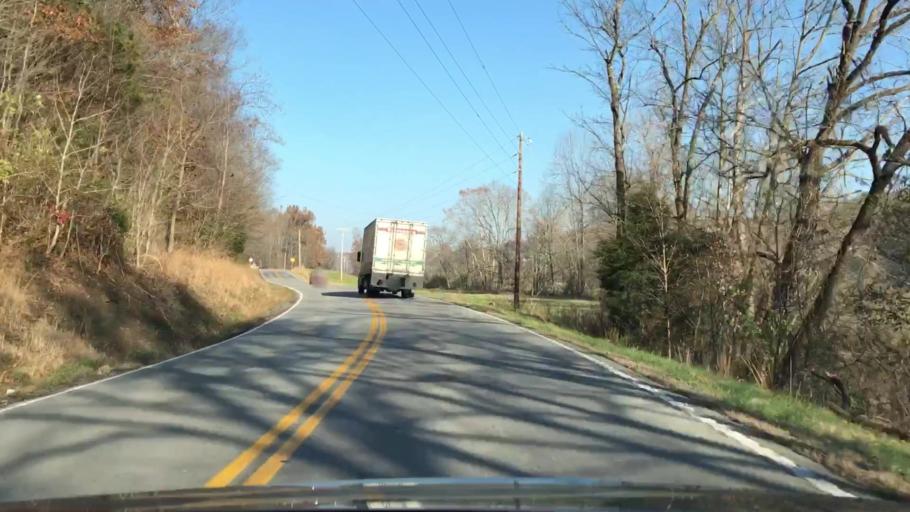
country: US
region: Kentucky
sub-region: Grayson County
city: Leitchfield
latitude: 37.4378
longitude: -86.2834
